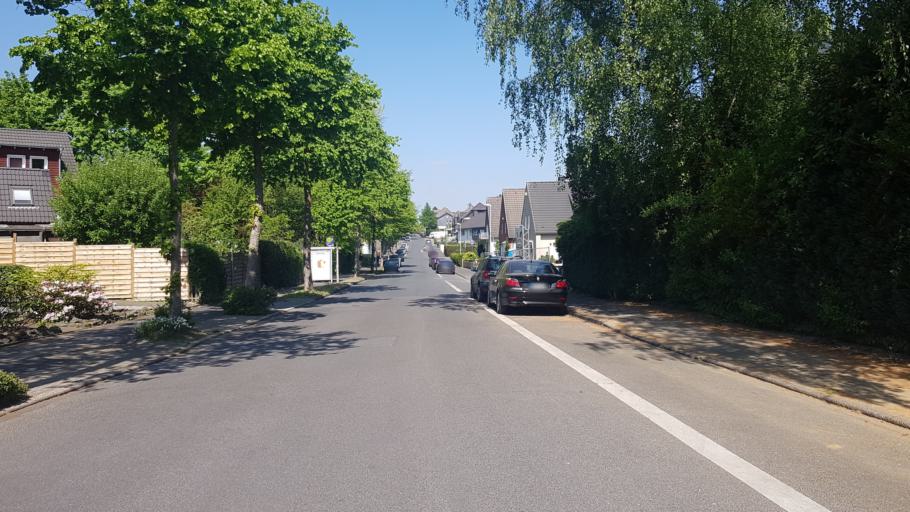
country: DE
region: North Rhine-Westphalia
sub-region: Regierungsbezirk Dusseldorf
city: Muelheim (Ruhr)
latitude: 51.4153
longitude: 6.8401
